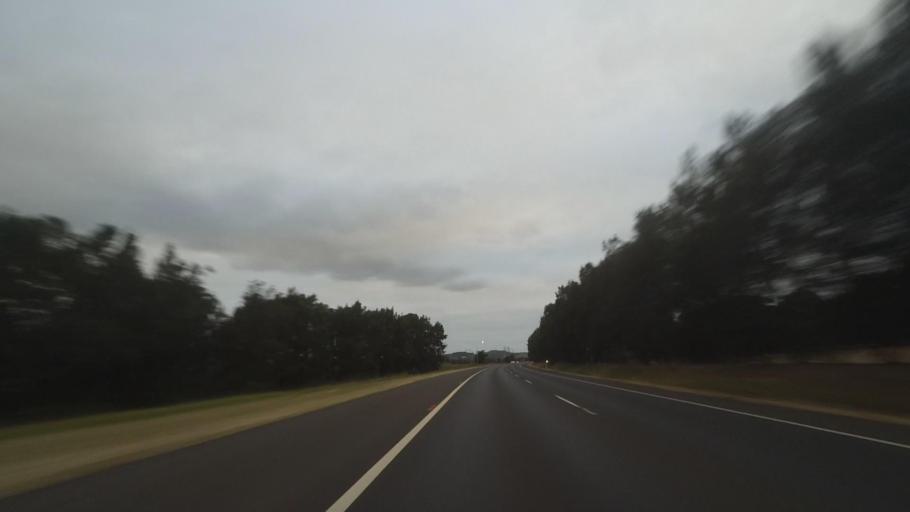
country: AU
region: New South Wales
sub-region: Wollongong
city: Koonawarra
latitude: -34.4871
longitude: 150.8097
